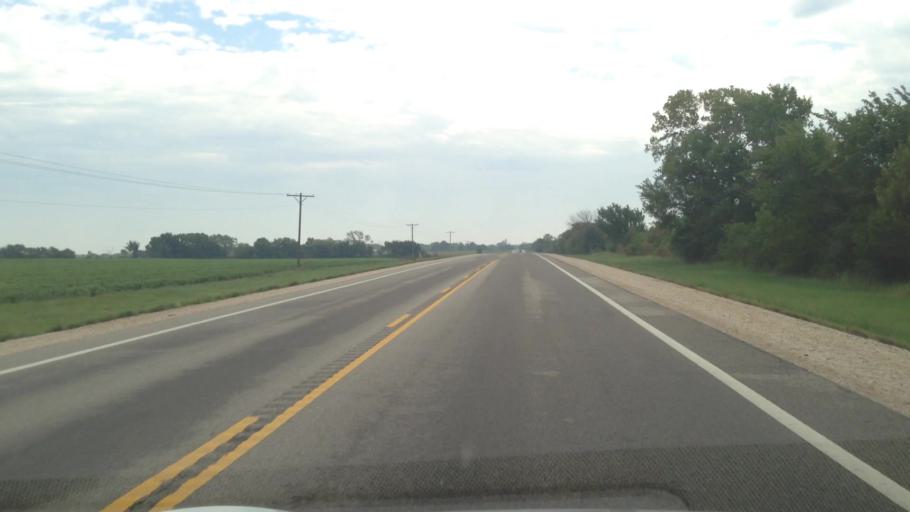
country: US
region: Kansas
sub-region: Allen County
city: Iola
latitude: 37.9054
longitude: -95.0950
